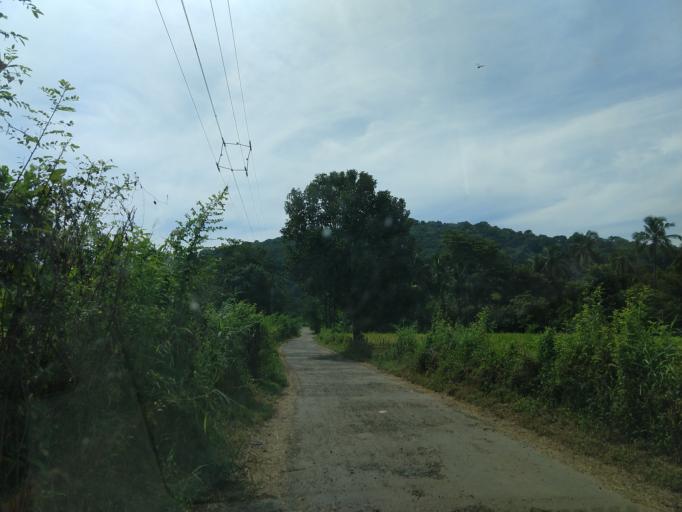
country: IN
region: Maharashtra
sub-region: Sindhudurg
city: Savantvadi
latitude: 15.9749
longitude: 73.7870
